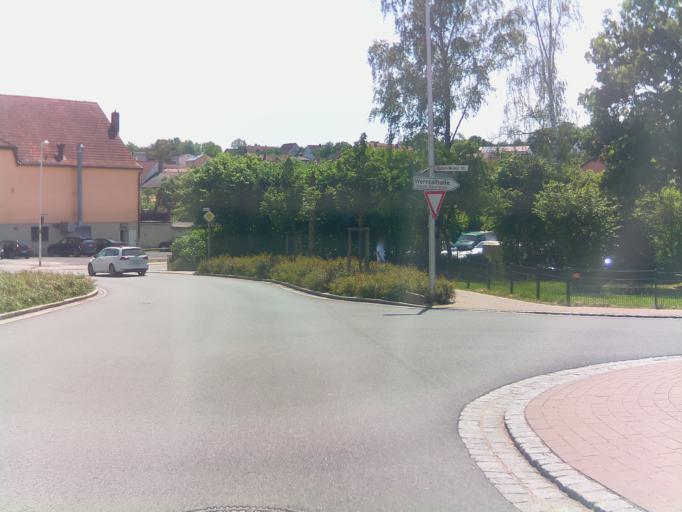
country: DE
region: Bavaria
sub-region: Regierungsbezirk Unterfranken
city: Poppenhausen
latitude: 50.1025
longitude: 10.1430
